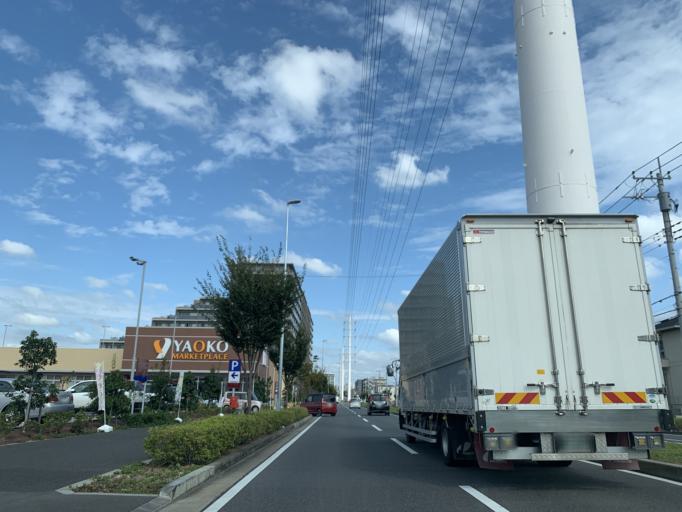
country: JP
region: Chiba
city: Nagareyama
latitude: 35.8641
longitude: 139.9205
